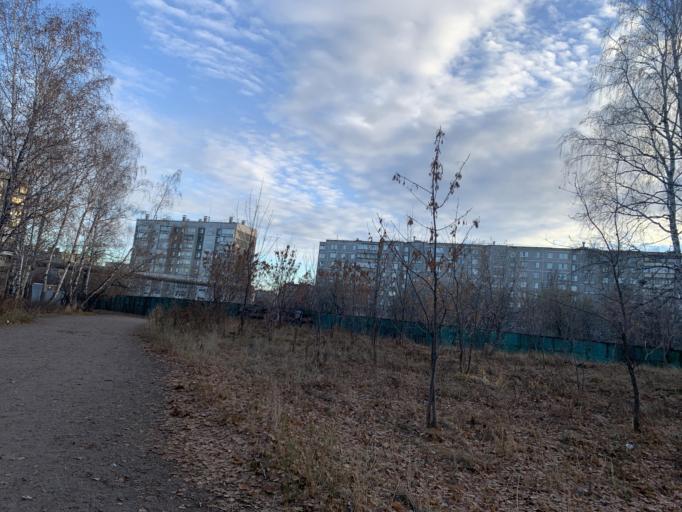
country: RU
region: Chelyabinsk
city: Roshchino
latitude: 55.1998
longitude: 61.3107
